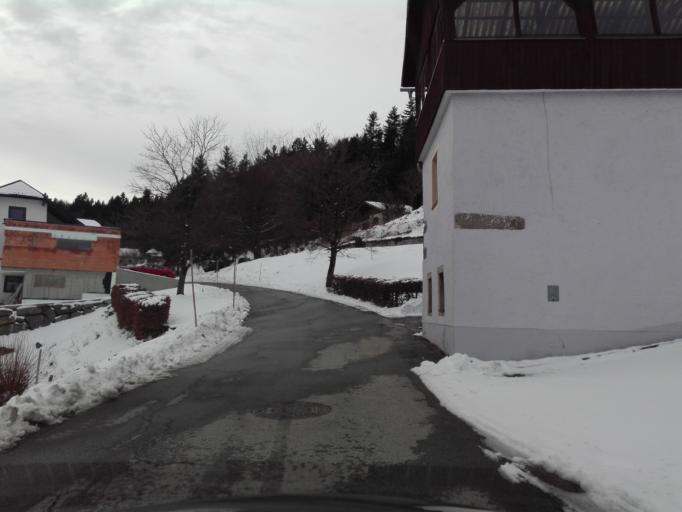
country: AT
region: Upper Austria
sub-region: Politischer Bezirk Rohrbach
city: Pfarrkirchen im Muehlkreis
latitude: 48.5528
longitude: 13.8418
